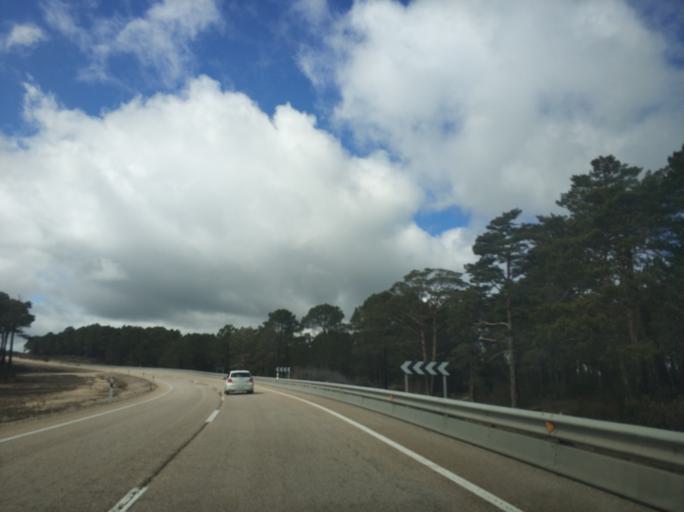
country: ES
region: Castille and Leon
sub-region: Provincia de Soria
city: Muriel Viejo
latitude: 41.8185
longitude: -2.9208
